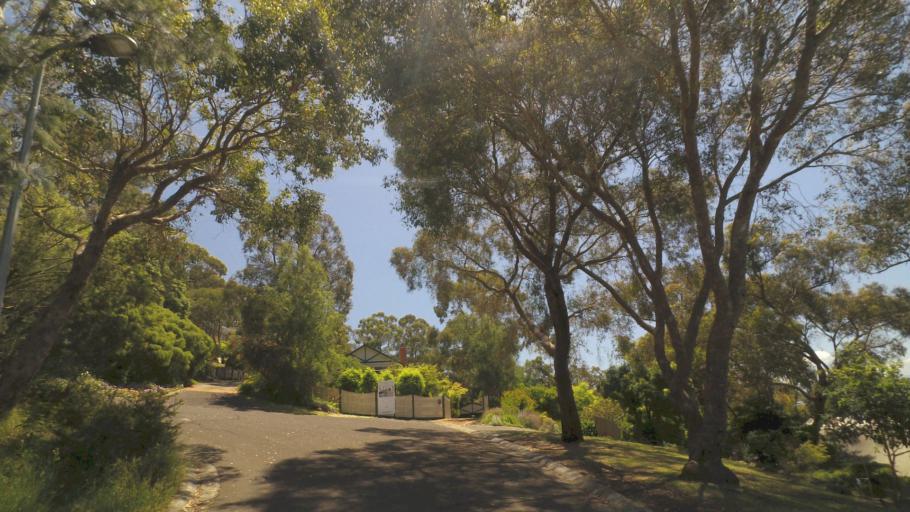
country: AU
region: Victoria
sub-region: Maroondah
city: Croydon North
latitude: -37.7744
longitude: 145.2837
